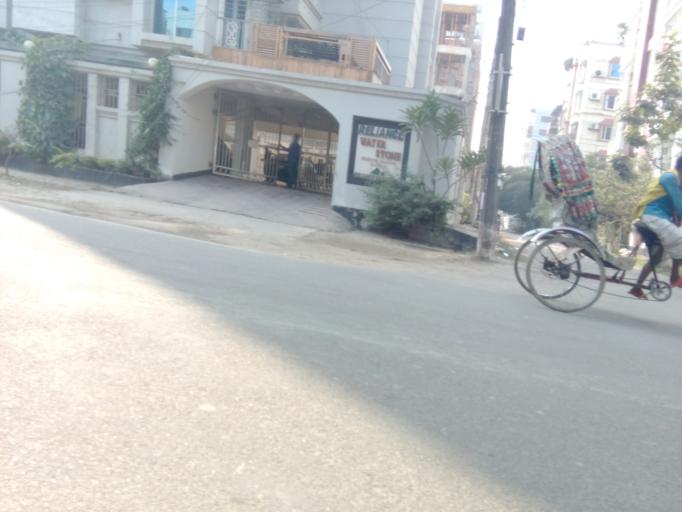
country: BD
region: Dhaka
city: Tungi
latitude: 23.8177
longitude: 90.4340
